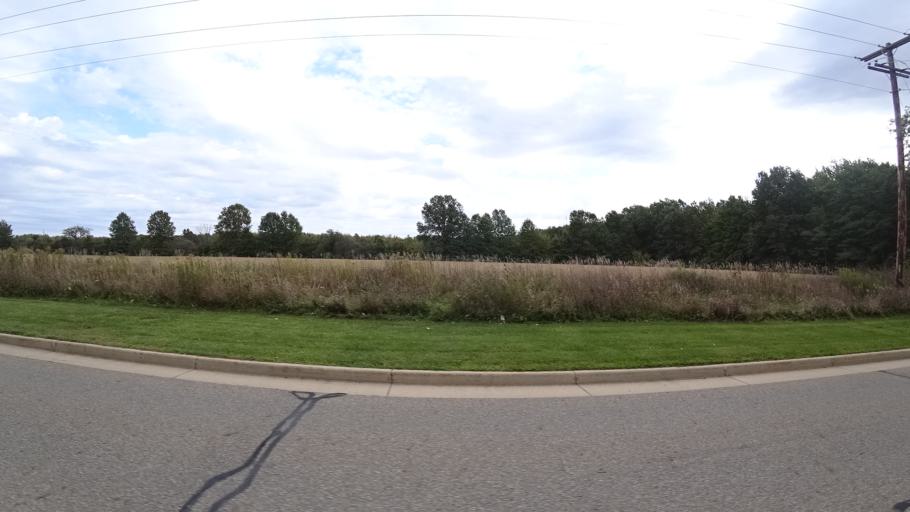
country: US
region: Indiana
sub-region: LaPorte County
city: Trail Creek
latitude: 41.6736
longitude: -86.8844
